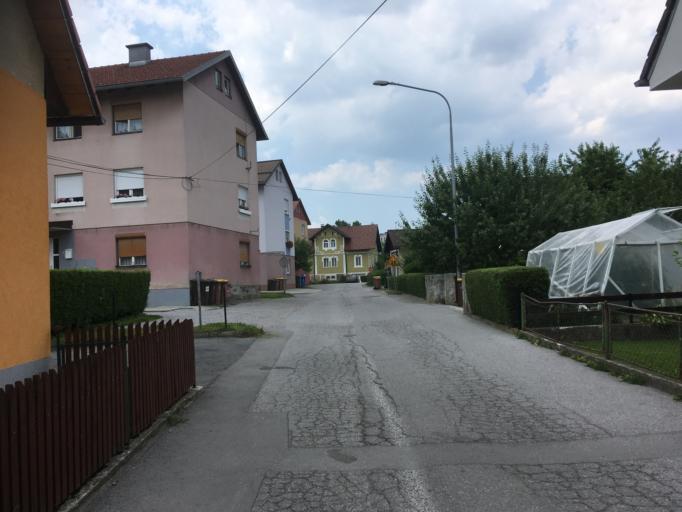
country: SI
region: Kocevje
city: Kocevje
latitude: 45.6406
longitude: 14.8557
